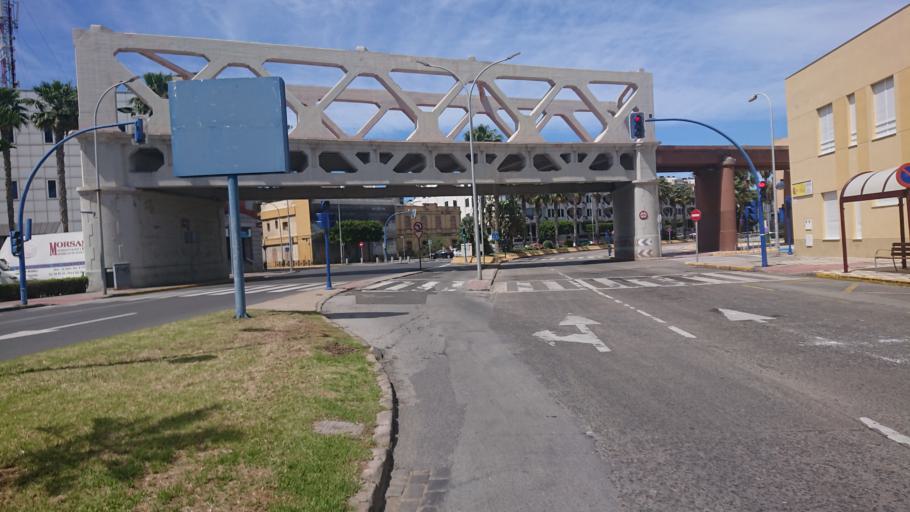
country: ES
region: Melilla
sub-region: Melilla
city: Melilla
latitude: 35.2892
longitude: -2.9398
